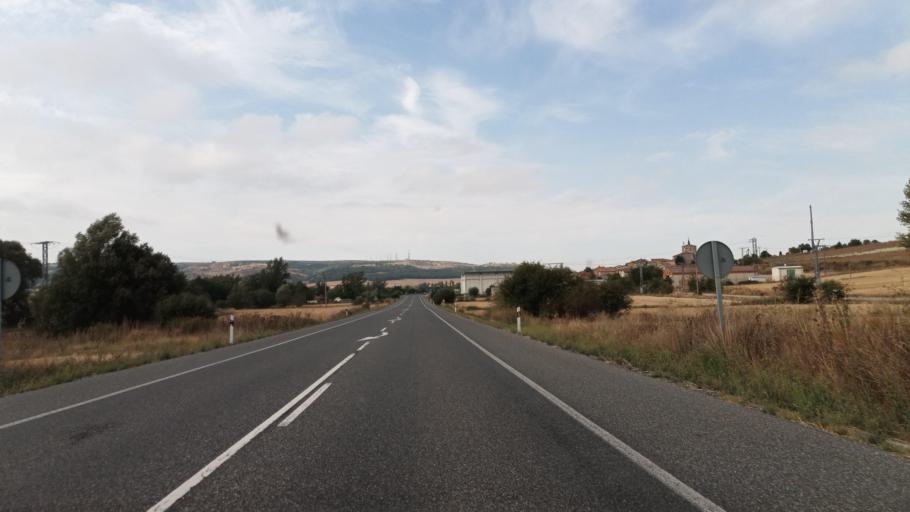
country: ES
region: Castille and Leon
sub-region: Provincia de Burgos
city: Quintanapalla
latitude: 42.4120
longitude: -3.5286
